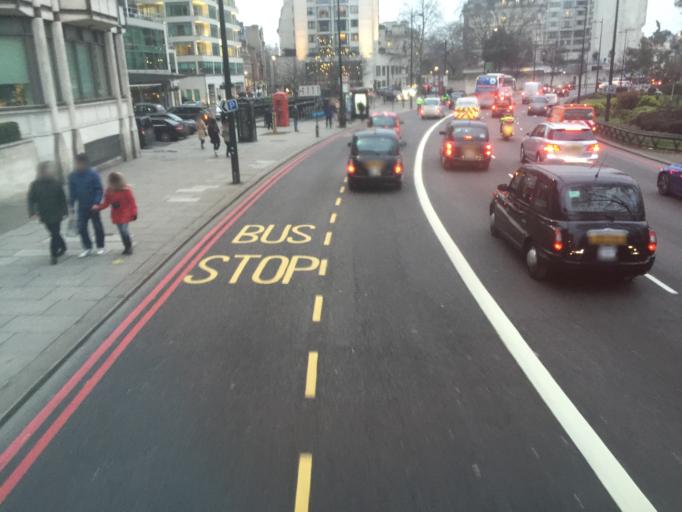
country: GB
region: England
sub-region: Greater London
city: London
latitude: 51.5059
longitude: -0.1513
